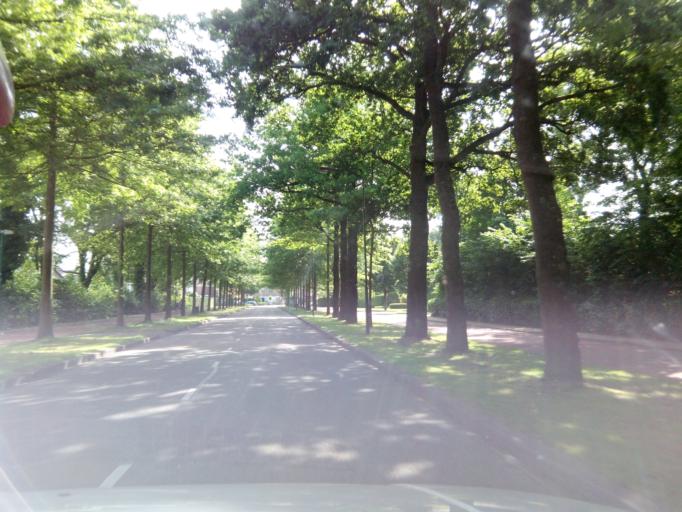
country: NL
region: Utrecht
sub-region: Gemeente Woudenberg
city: Woudenberg
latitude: 52.0822
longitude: 5.4073
